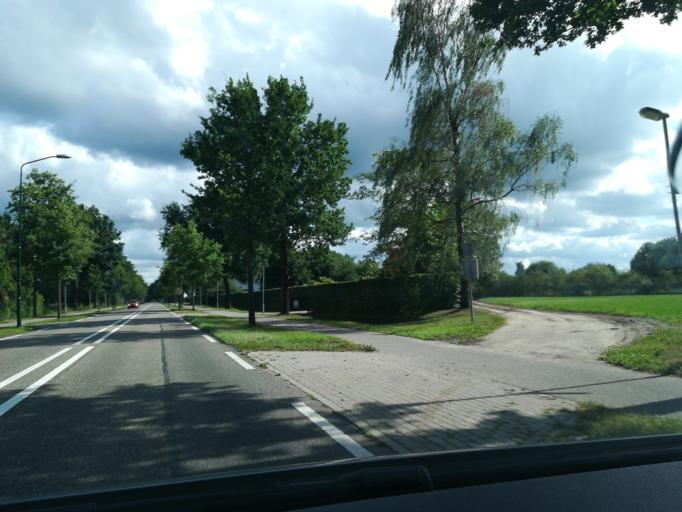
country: NL
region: North Brabant
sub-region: Gemeente Waalre
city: Waalre
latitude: 51.3974
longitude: 5.4345
